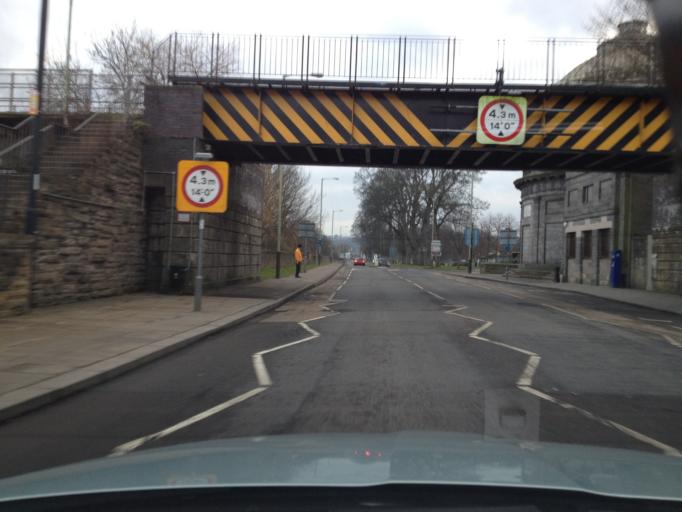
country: GB
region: Scotland
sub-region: Perth and Kinross
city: Perth
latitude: 56.3927
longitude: -3.4261
